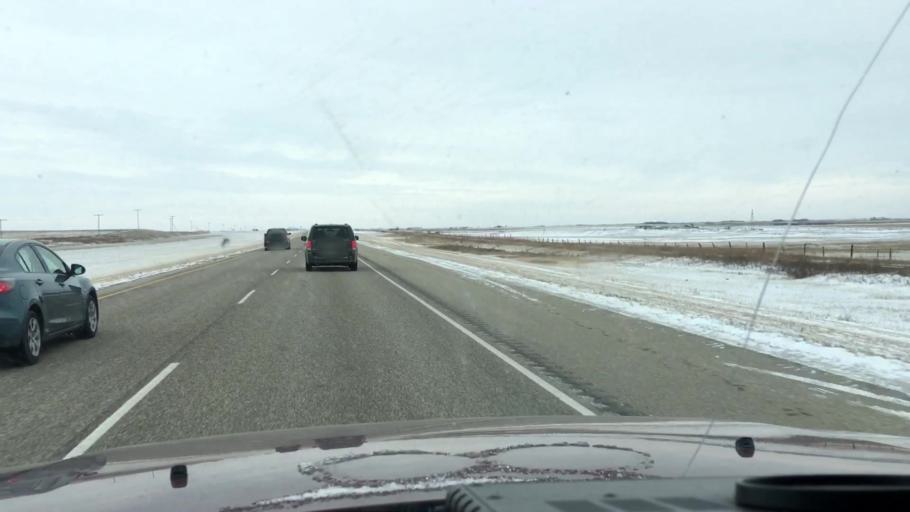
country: CA
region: Saskatchewan
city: Saskatoon
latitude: 51.5952
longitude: -106.3878
